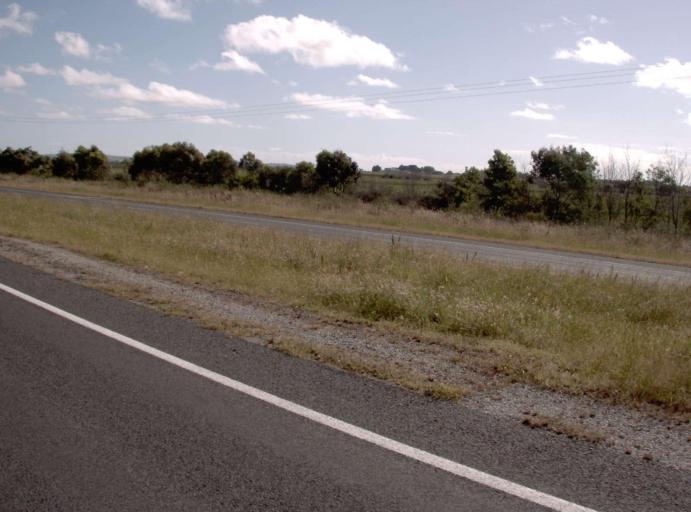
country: AU
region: Victoria
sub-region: Bass Coast
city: North Wonthaggi
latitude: -38.4479
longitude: 145.4823
